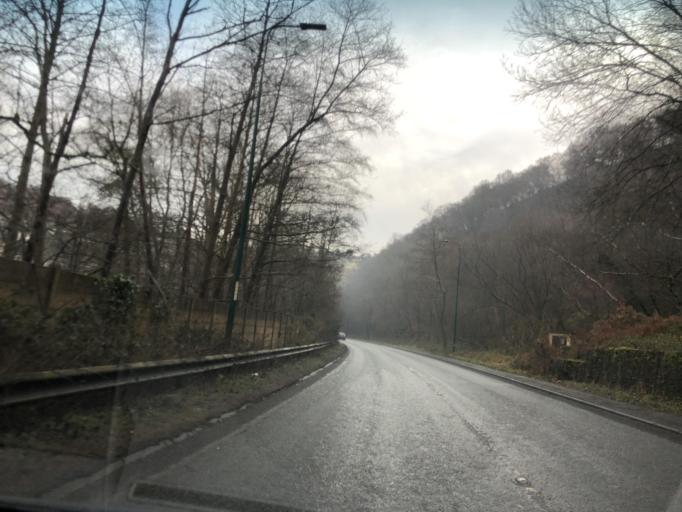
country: GB
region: Wales
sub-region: Caerphilly County Borough
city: Crumlin
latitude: 51.6995
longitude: -3.1391
